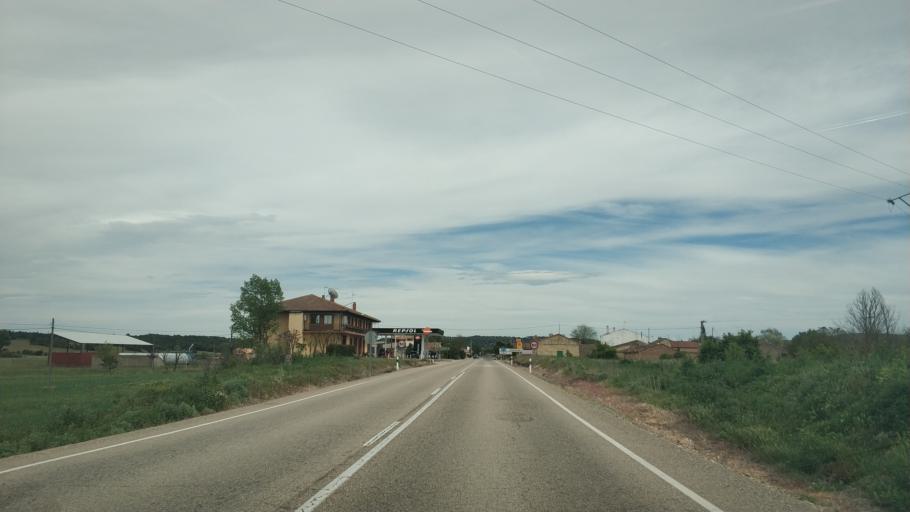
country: ES
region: Castille and Leon
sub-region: Provincia de Soria
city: Berlanga de Duero
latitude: 41.4963
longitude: -2.8726
